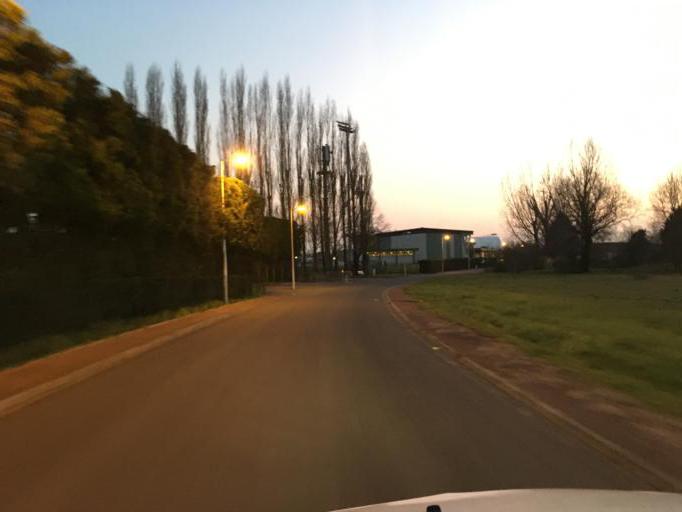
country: FR
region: Aquitaine
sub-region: Departement de la Gironde
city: Braud-et-Saint-Louis
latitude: 45.2519
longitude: -0.6263
